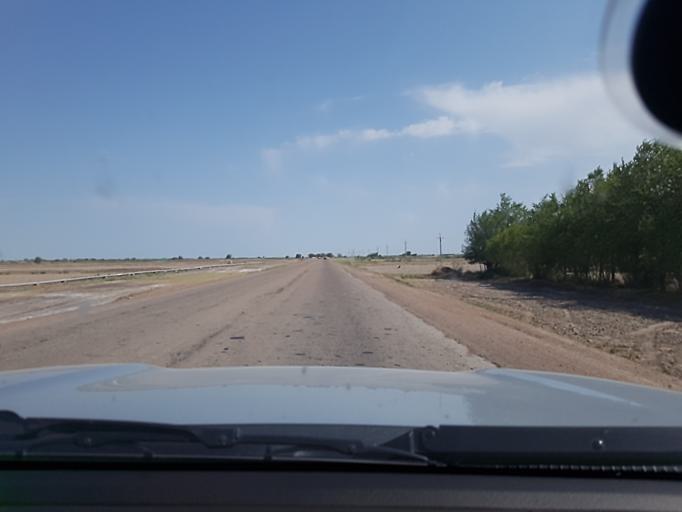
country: TM
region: Dasoguz
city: Boldumsaz
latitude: 42.1984
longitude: 59.5397
